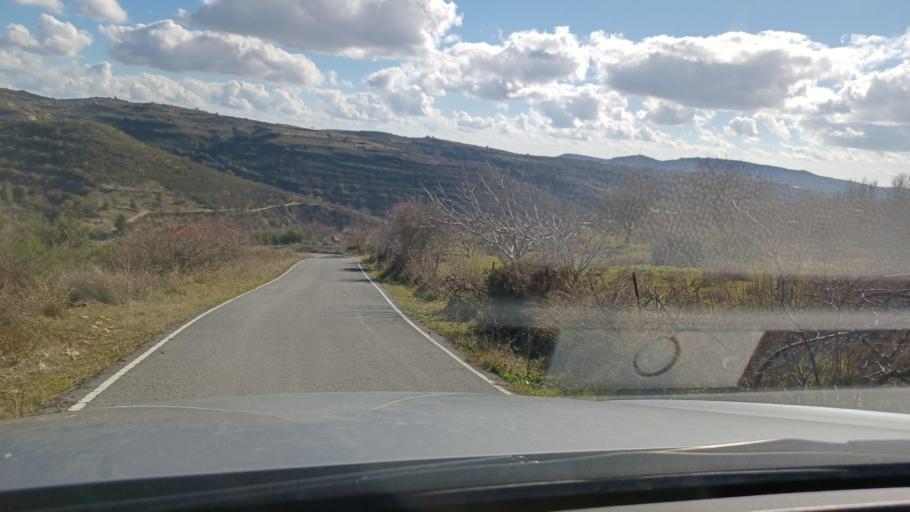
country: CY
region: Limassol
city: Pachna
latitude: 34.8263
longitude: 32.8066
